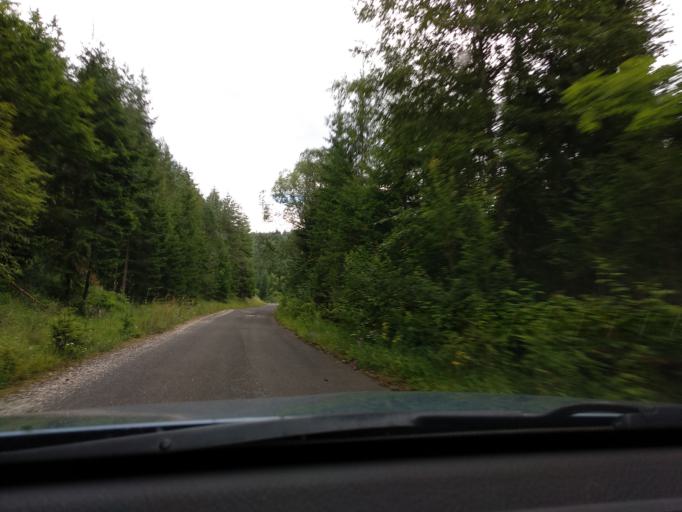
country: SK
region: Zilinsky
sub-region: Okres Liptovsky Mikulas
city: Hybe
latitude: 49.0243
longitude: 19.8737
